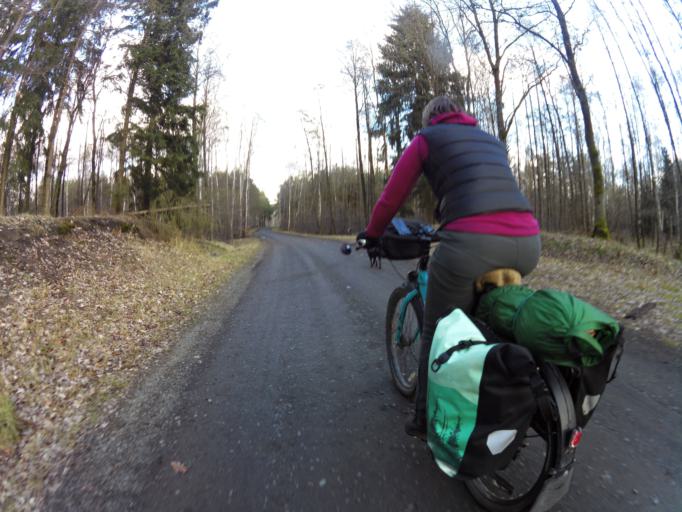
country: PL
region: West Pomeranian Voivodeship
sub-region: Powiat mysliborski
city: Debno
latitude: 52.7646
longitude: 14.7263
